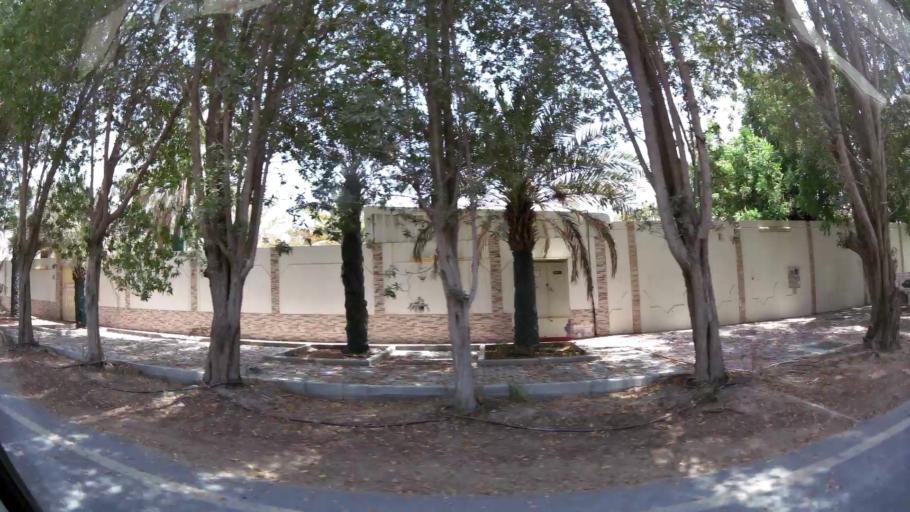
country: AE
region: Ash Shariqah
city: Sharjah
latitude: 25.2553
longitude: 55.4601
